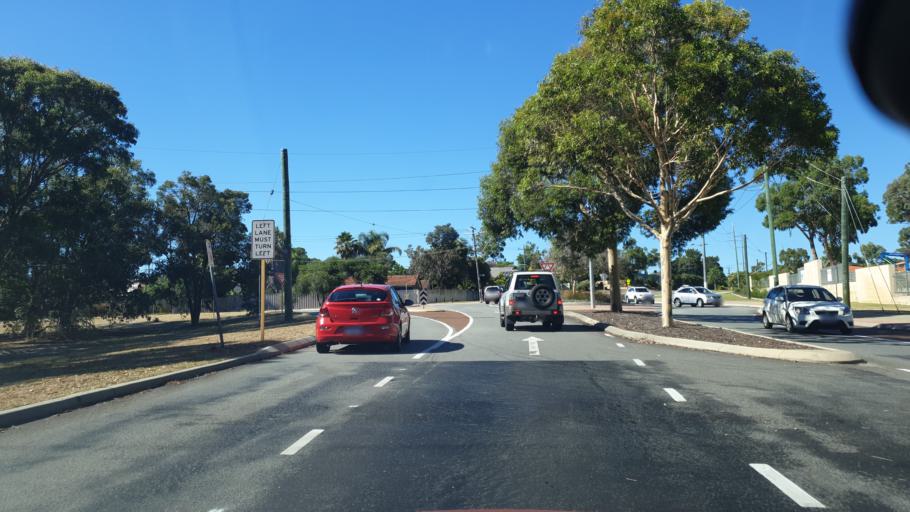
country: AU
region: Western Australia
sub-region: Canning
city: Rossmoyne
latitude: -32.0486
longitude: 115.8597
